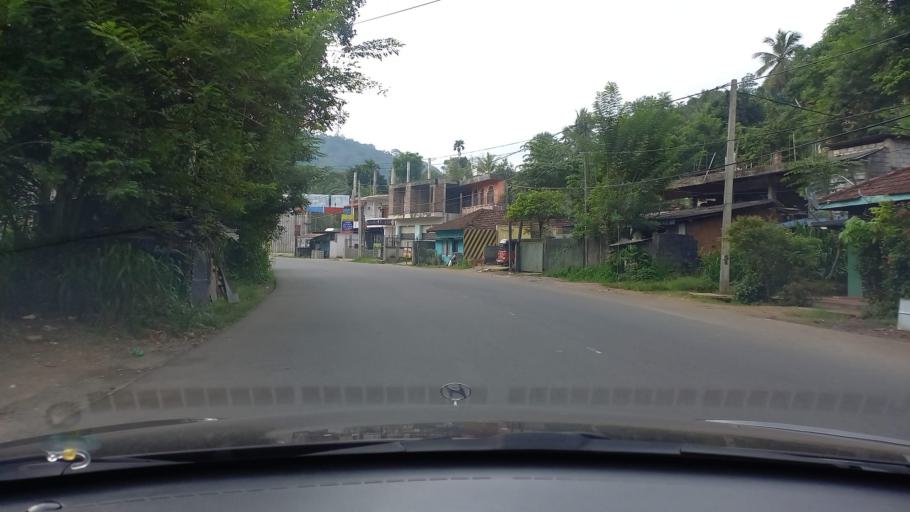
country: LK
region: Central
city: Kadugannawa
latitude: 7.2478
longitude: 80.4720
